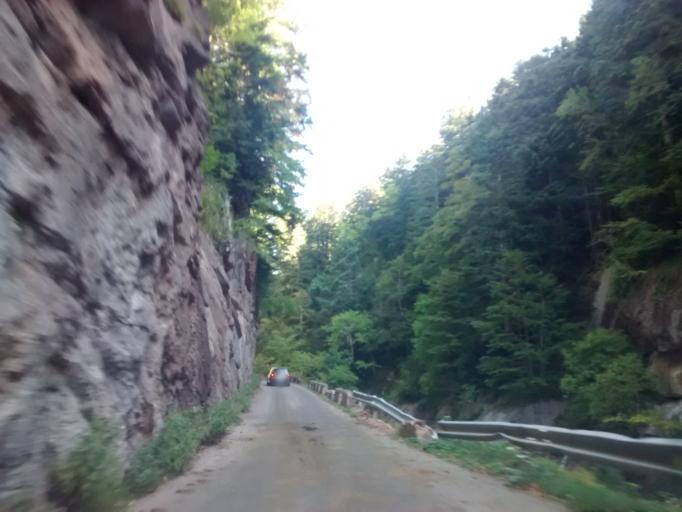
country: ES
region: Aragon
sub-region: Provincia de Huesca
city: Aragues del Puerto
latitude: 42.8265
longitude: -0.7114
